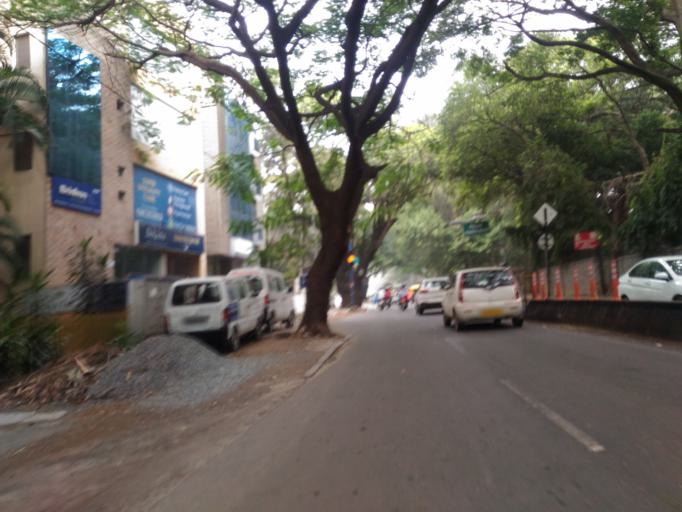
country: IN
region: Karnataka
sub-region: Bangalore Urban
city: Bangalore
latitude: 12.9573
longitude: 77.6059
